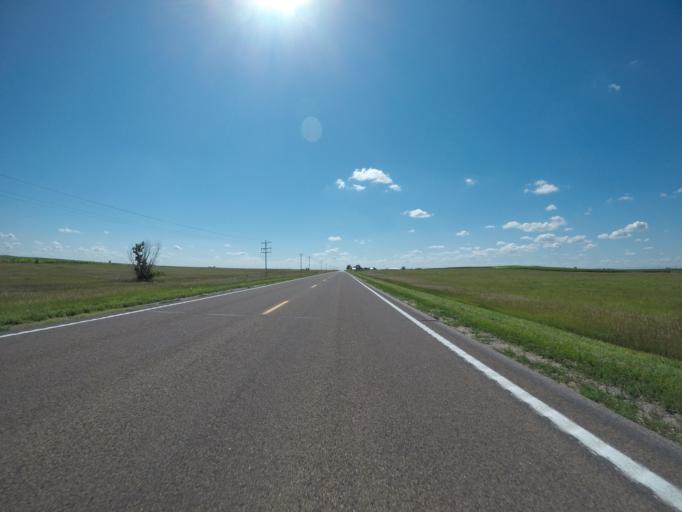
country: US
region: Nebraska
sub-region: Chase County
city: Imperial
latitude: 40.5376
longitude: -101.8449
